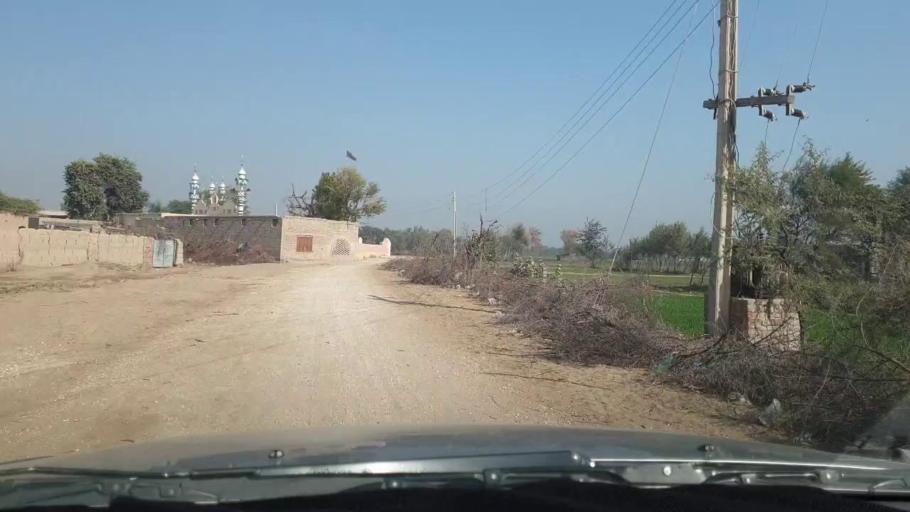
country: PK
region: Sindh
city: Khanpur
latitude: 27.8083
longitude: 69.5617
